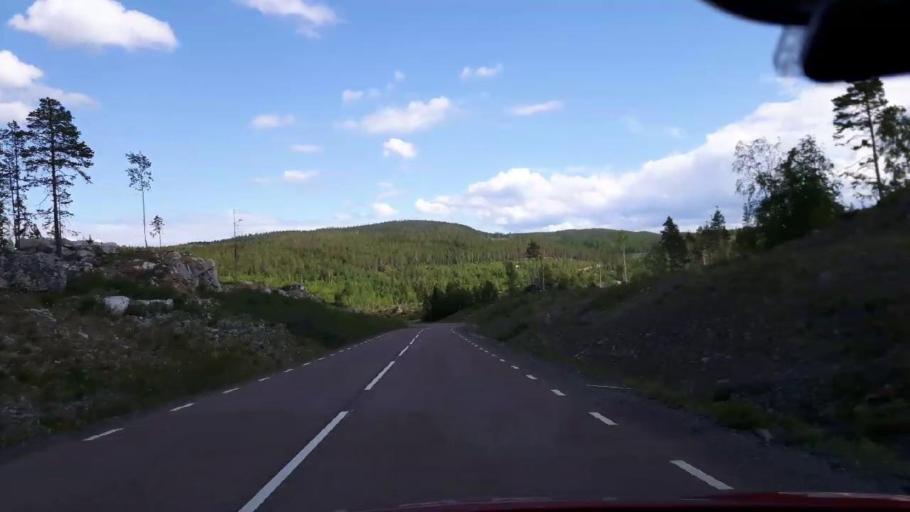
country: SE
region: Jaemtland
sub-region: Krokoms Kommun
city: Valla
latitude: 64.0446
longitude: 14.1859
